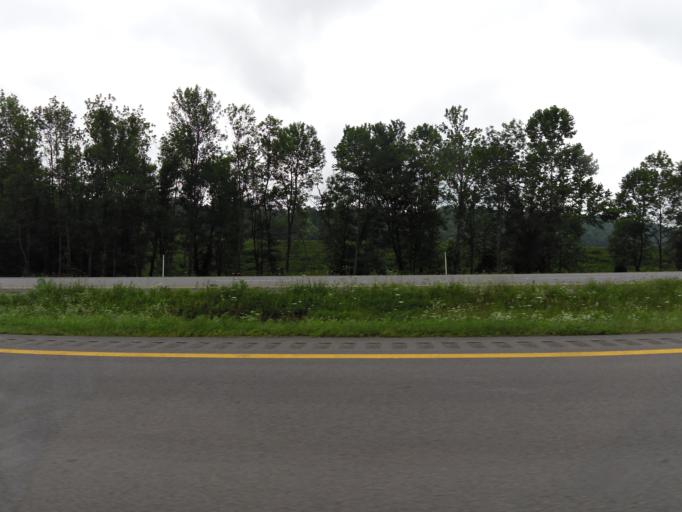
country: US
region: Kentucky
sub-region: Grayson County
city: Leitchfield
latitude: 37.4127
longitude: -86.4242
